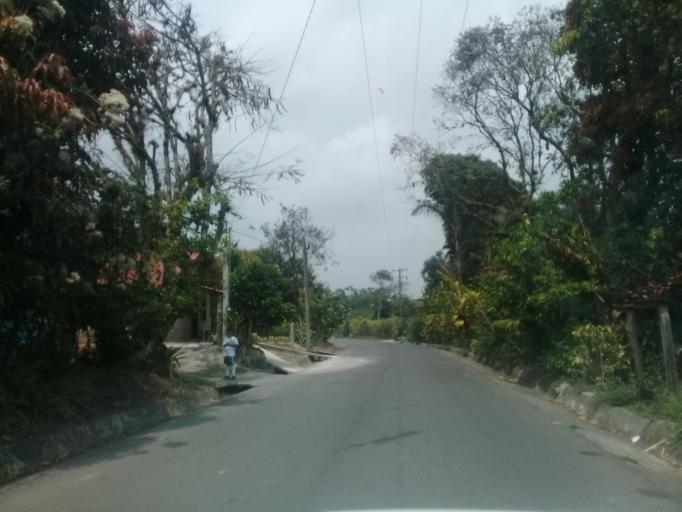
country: MX
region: Veracruz
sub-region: Cordoba
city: Fredepo
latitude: 18.8651
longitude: -96.9932
